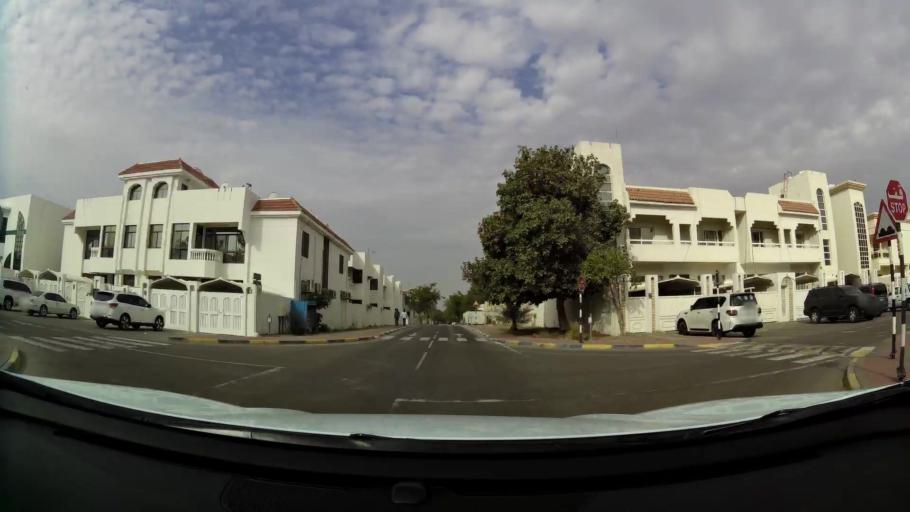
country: AE
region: Abu Dhabi
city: Al Ain
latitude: 24.2220
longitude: 55.7446
